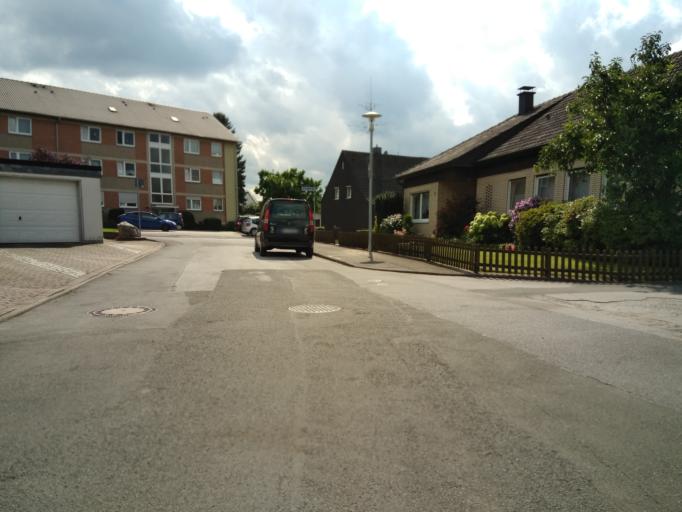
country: DE
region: North Rhine-Westphalia
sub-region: Regierungsbezirk Munster
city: Gladbeck
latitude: 51.5976
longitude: 6.9799
